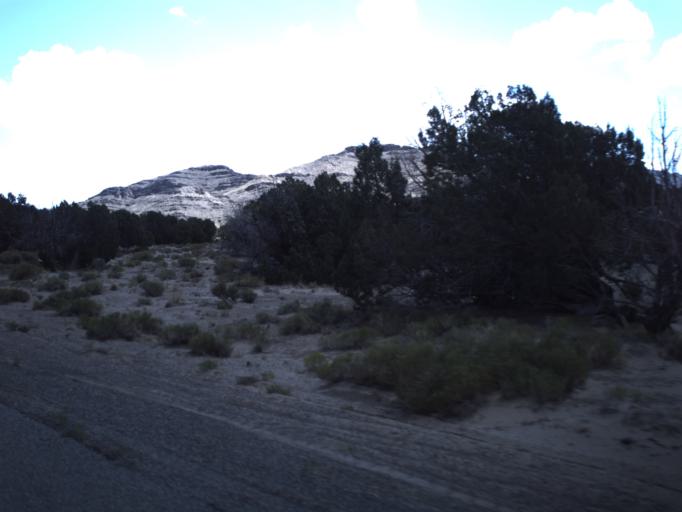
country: US
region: Utah
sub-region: Beaver County
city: Milford
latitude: 39.0728
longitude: -113.7211
